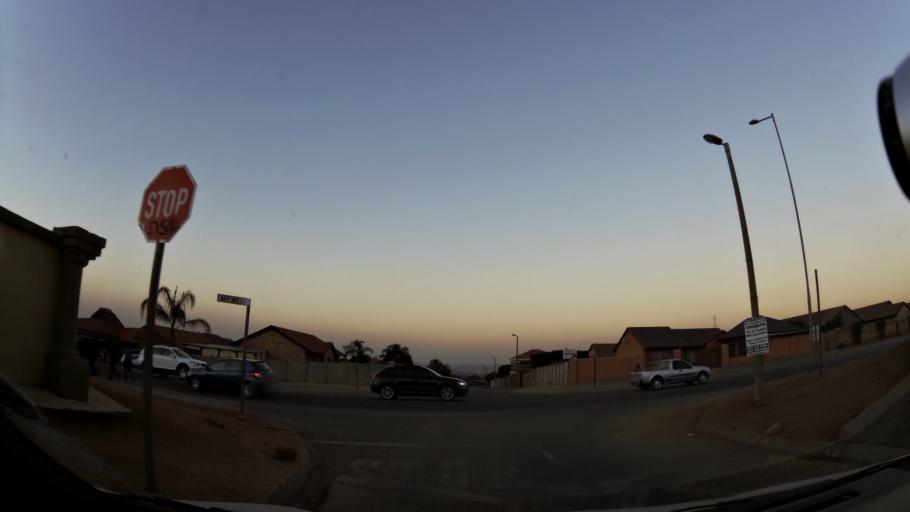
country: ZA
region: North-West
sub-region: Bojanala Platinum District Municipality
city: Rustenburg
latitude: -25.6530
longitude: 27.2020
